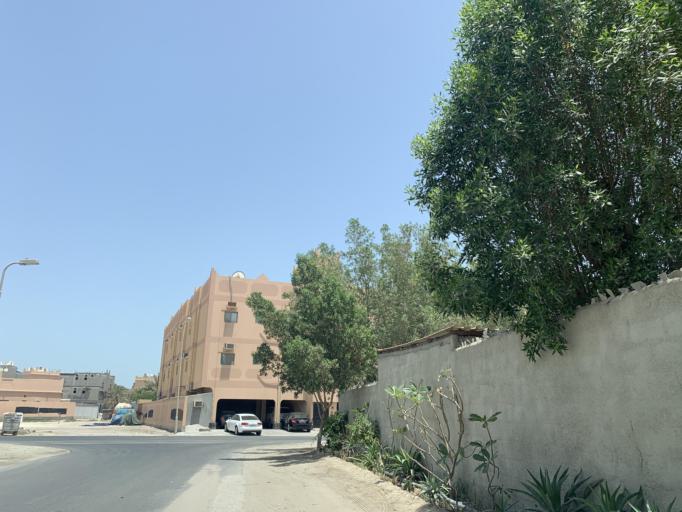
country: BH
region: Northern
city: Sitrah
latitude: 26.1721
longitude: 50.6071
